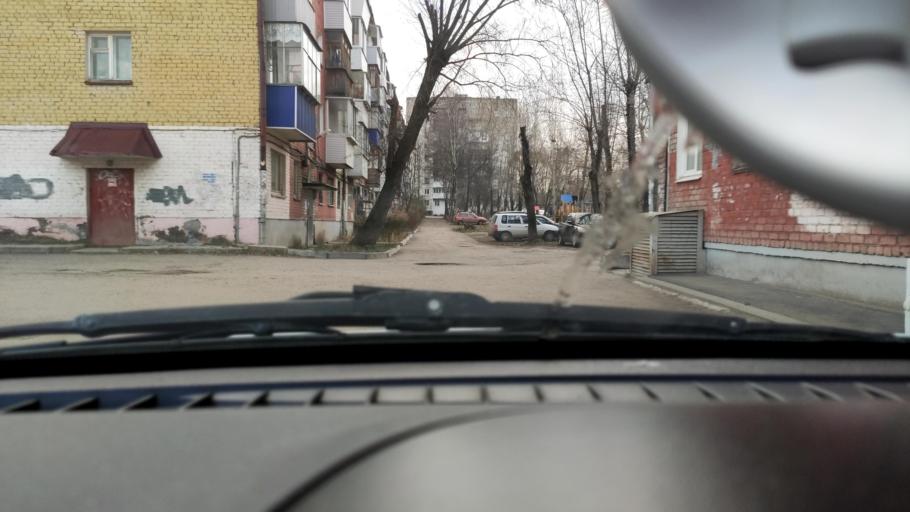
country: RU
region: Perm
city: Perm
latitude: 58.1036
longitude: 56.3858
